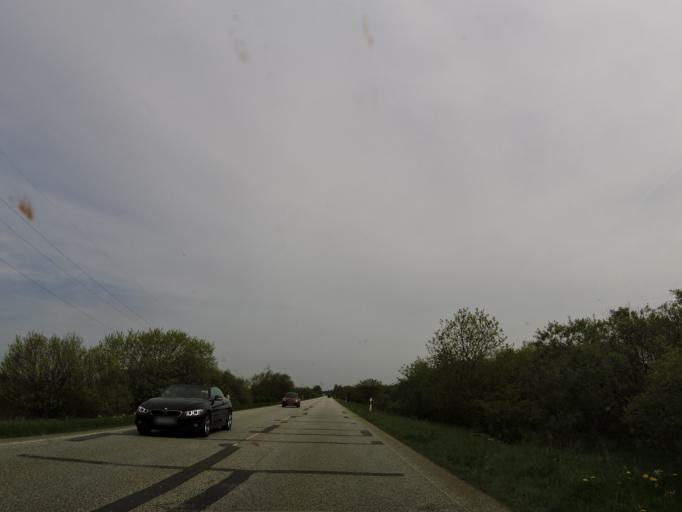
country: DE
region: Schleswig-Holstein
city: Husum
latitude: 54.4592
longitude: 9.0582
